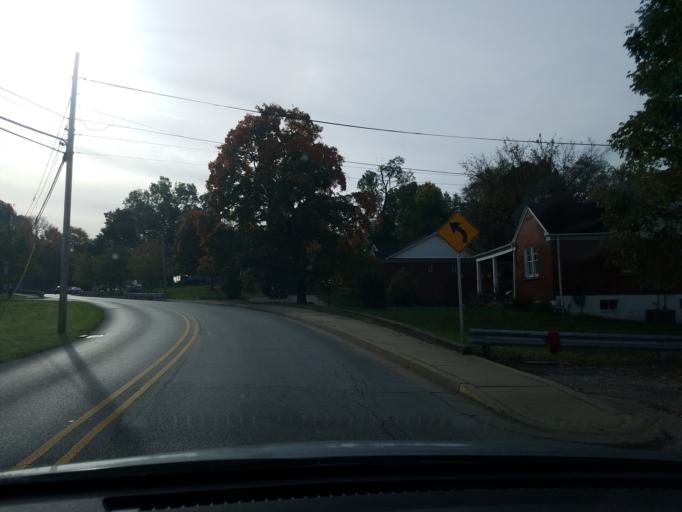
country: US
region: Indiana
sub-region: Floyd County
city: New Albany
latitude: 38.3051
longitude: -85.8207
